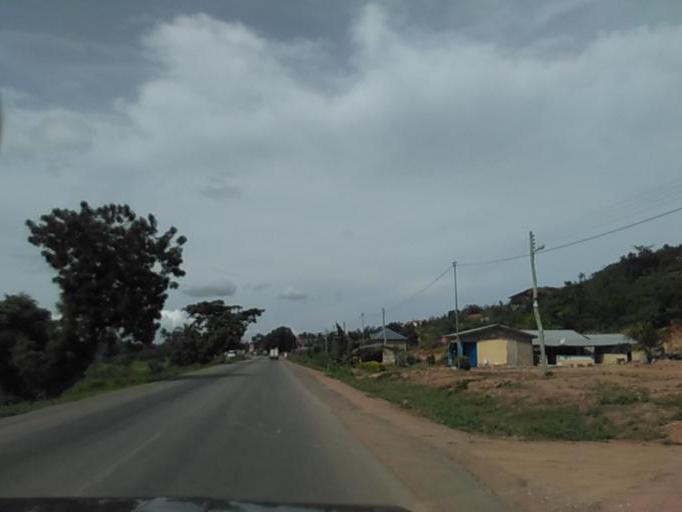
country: GH
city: Akropong
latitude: 6.2240
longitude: 0.0873
